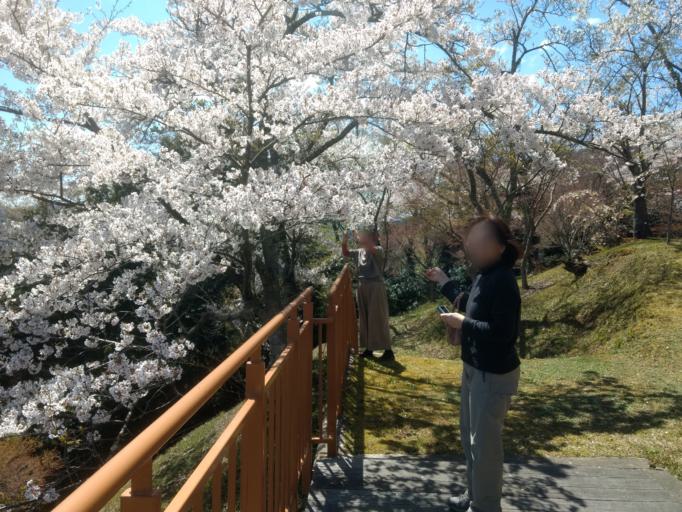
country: JP
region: Kyoto
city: Miyazu
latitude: 35.5764
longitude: 135.1870
